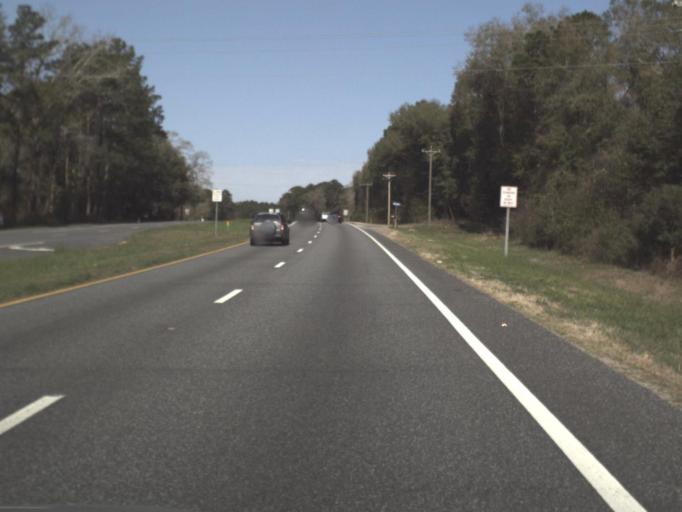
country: US
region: Florida
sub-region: Gadsden County
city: Midway
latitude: 30.5338
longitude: -84.3633
